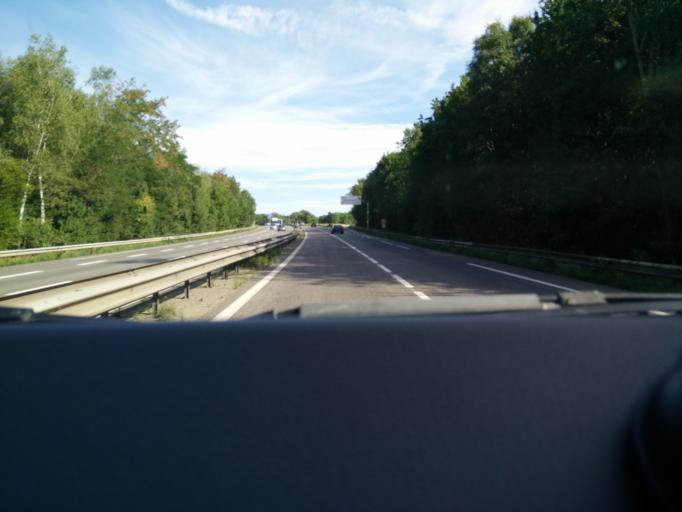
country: FR
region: Lorraine
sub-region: Departement de Meurthe-et-Moselle
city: Chavigny
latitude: 48.6486
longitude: 6.1352
